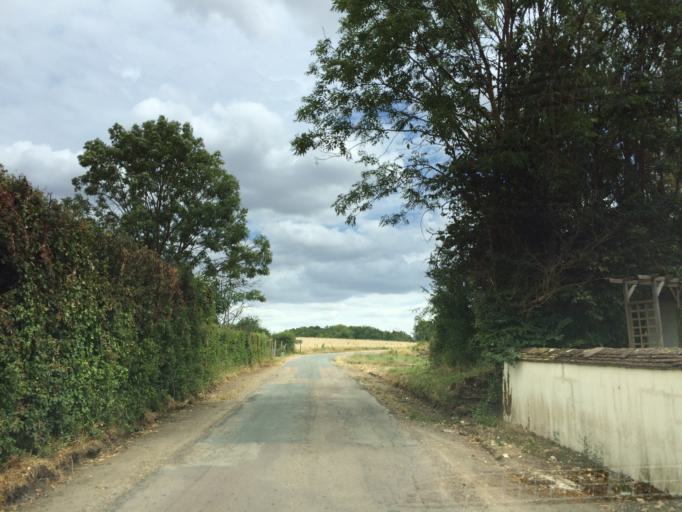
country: FR
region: Bourgogne
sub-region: Departement de l'Yonne
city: Fleury-la-Vallee
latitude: 47.8465
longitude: 3.4082
